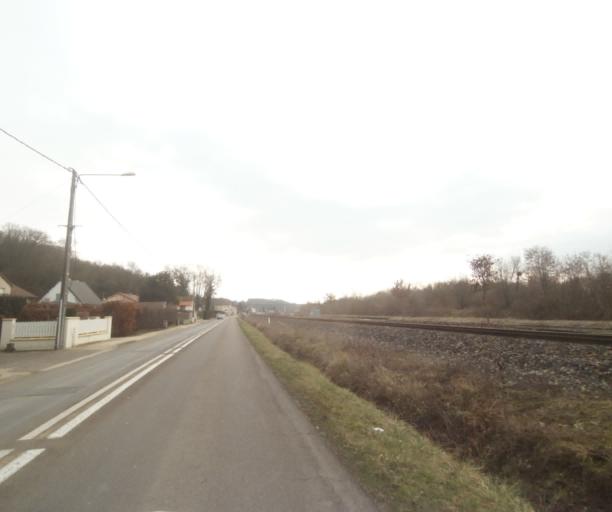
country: FR
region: Champagne-Ardenne
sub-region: Departement de la Haute-Marne
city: Bettancourt-la-Ferree
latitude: 48.6324
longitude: 4.9836
